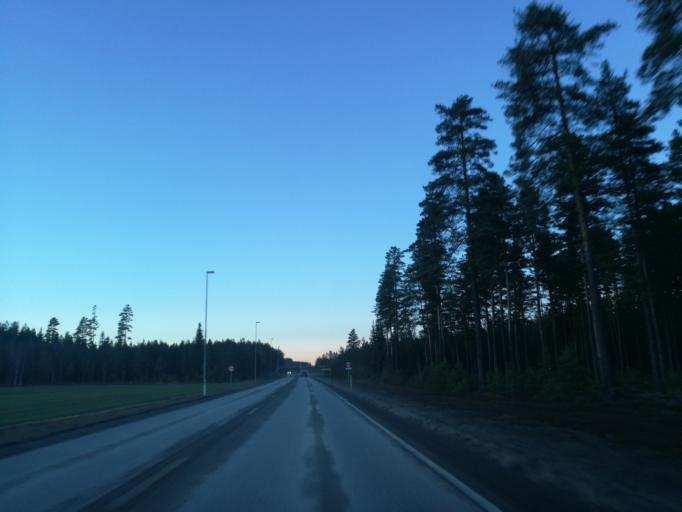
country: NO
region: Hedmark
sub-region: Eidskog
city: Skotterud
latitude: 59.9537
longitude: 12.1674
